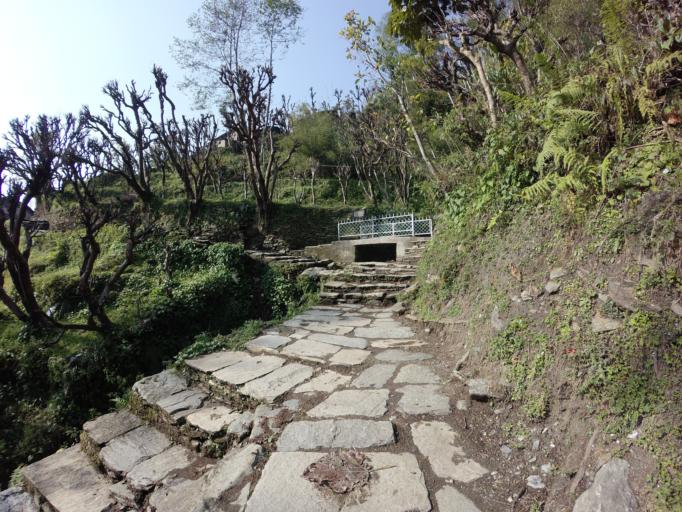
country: NP
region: Western Region
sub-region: Dhawalagiri Zone
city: Chitre
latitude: 28.3789
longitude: 83.8070
